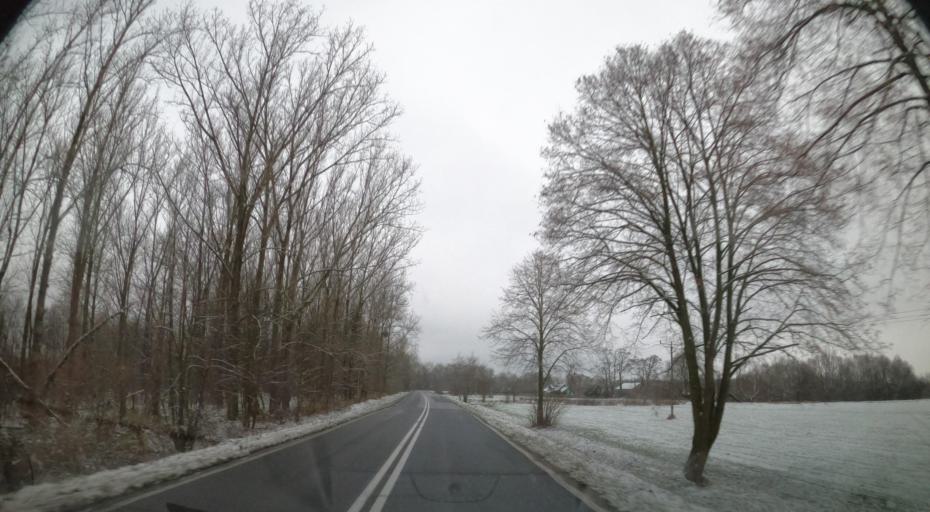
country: PL
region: Masovian Voivodeship
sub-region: Powiat plocki
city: Nowy Duninow
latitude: 52.5791
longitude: 19.5390
